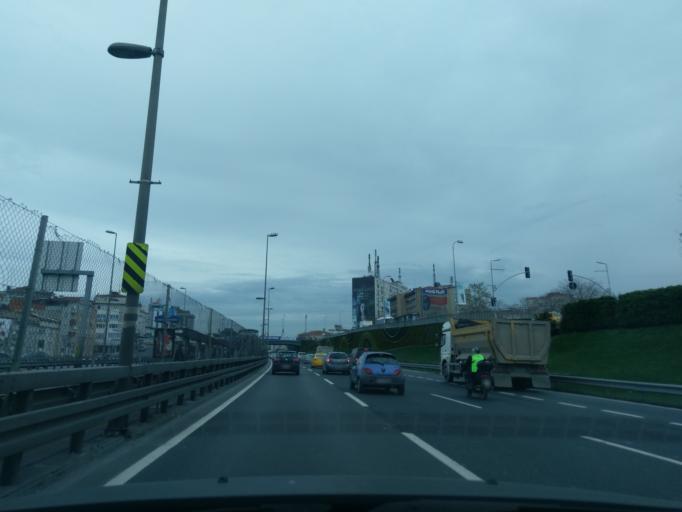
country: TR
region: Istanbul
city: Sisli
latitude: 41.0616
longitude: 28.9672
